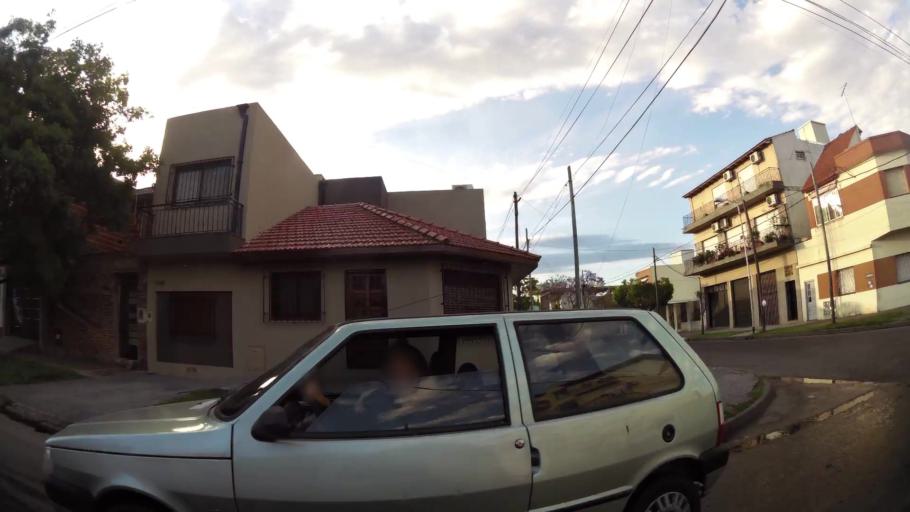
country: AR
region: Buenos Aires
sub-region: Partido de Avellaneda
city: Avellaneda
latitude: -34.6925
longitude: -58.3353
